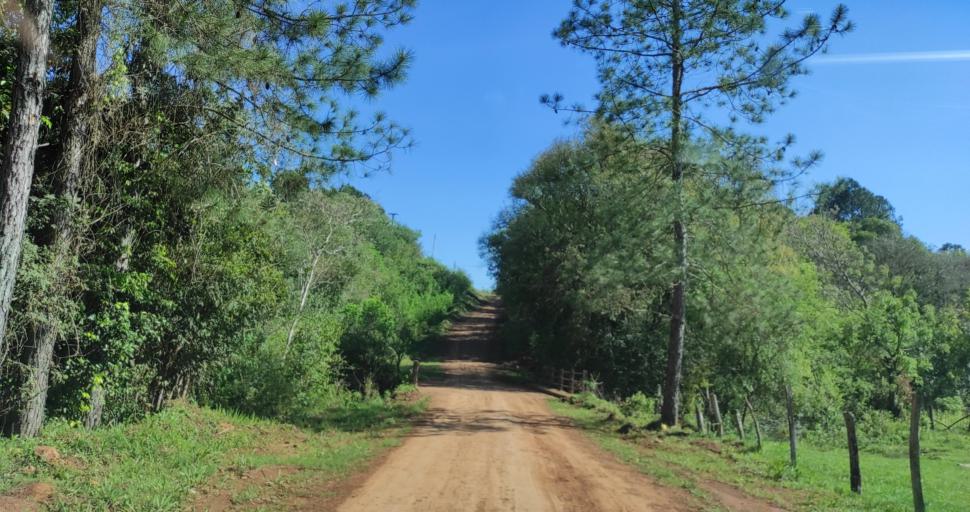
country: AR
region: Misiones
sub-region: Departamento de Candelaria
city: Loreto
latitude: -27.3224
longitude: -55.5297
